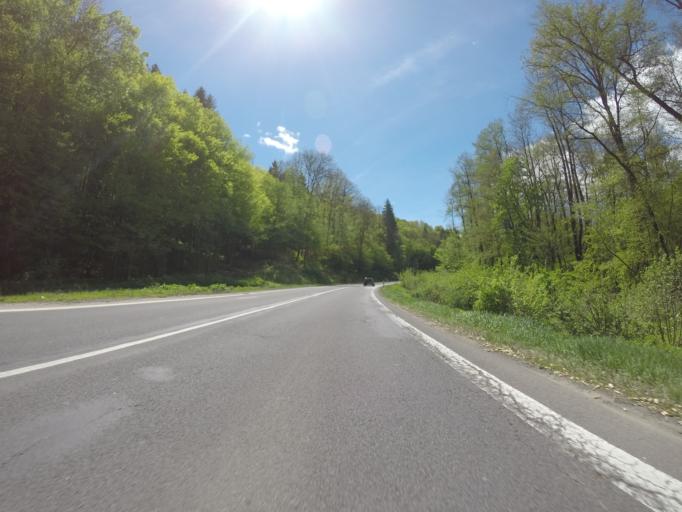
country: SK
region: Banskobystricky
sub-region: Okres Banska Bystrica
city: Zvolen
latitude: 48.5381
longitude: 19.1229
